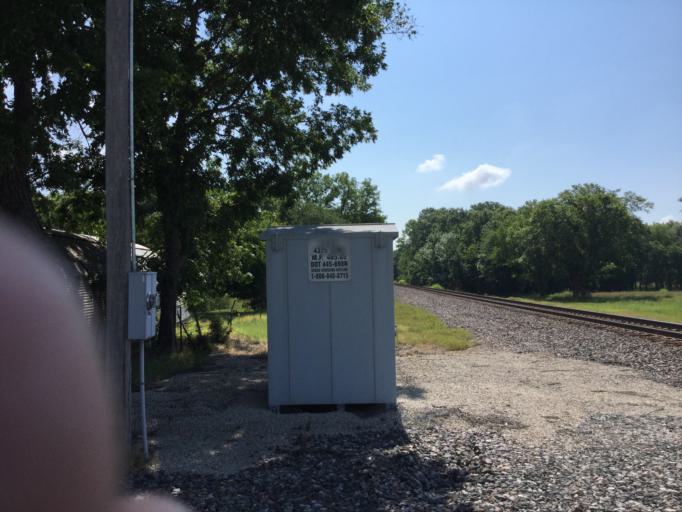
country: US
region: Kansas
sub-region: Montgomery County
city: Coffeyville
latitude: 37.0355
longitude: -95.6700
